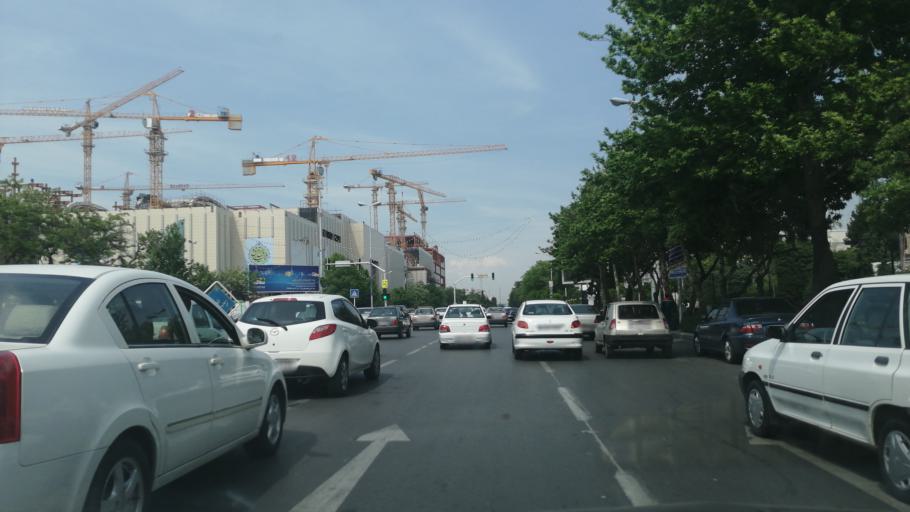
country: IR
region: Razavi Khorasan
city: Mashhad
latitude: 36.3142
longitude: 59.5597
